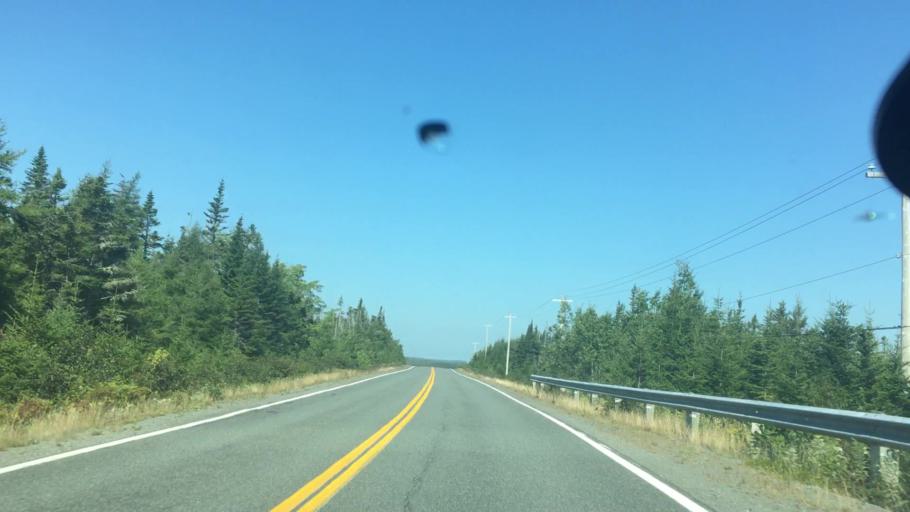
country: CA
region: Nova Scotia
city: Antigonish
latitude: 44.9902
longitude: -62.0958
